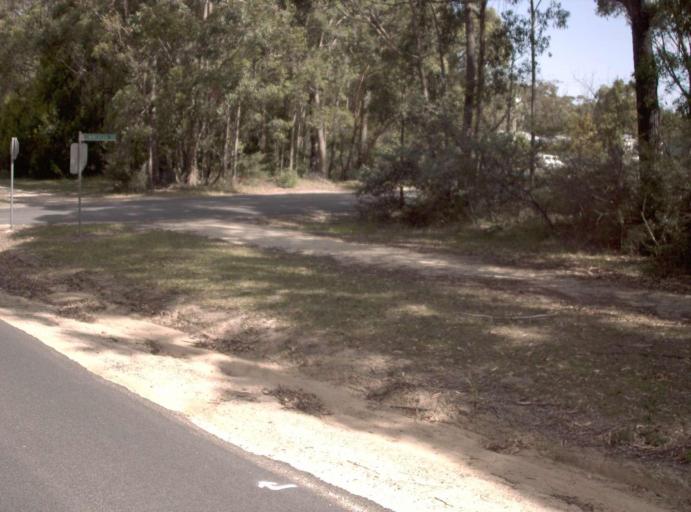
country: AU
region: New South Wales
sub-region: Bega Valley
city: Eden
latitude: -37.5551
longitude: 149.7438
